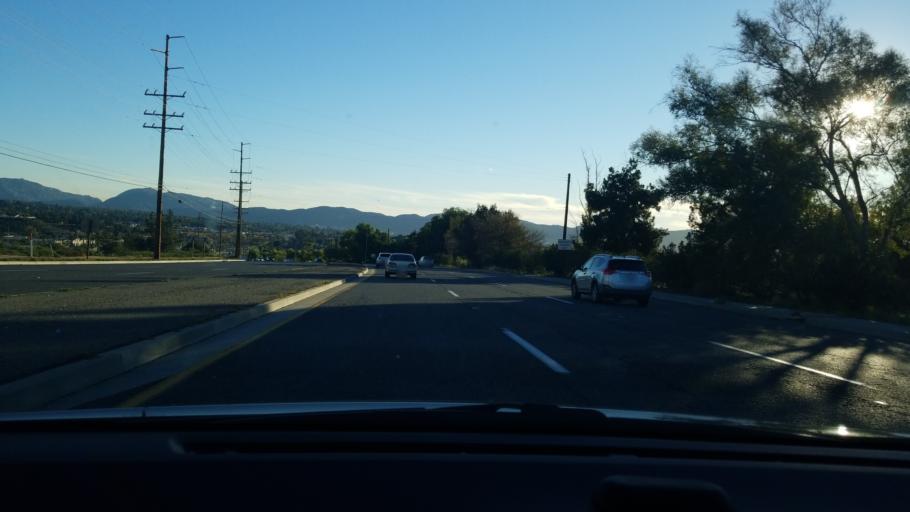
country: US
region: California
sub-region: Riverside County
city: Murrieta Hot Springs
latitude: 33.5591
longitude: -117.1395
